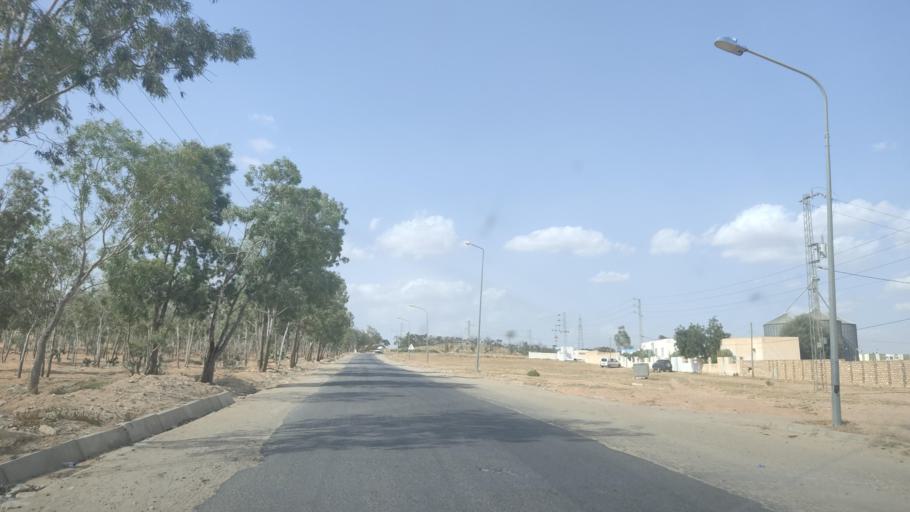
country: TN
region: Sidi Bu Zayd
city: Sidi Bouzid
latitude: 35.1067
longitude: 9.5380
